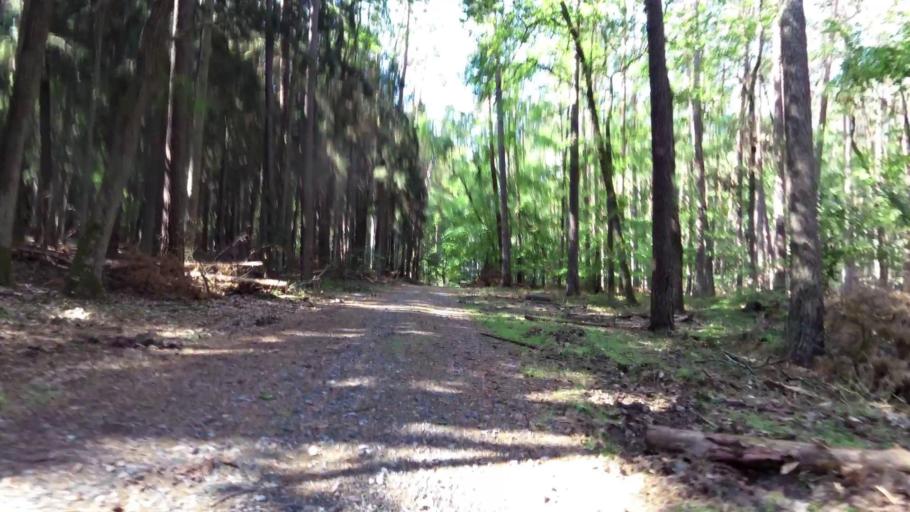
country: PL
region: West Pomeranian Voivodeship
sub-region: Powiat kamienski
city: Miedzyzdroje
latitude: 53.9100
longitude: 14.4769
